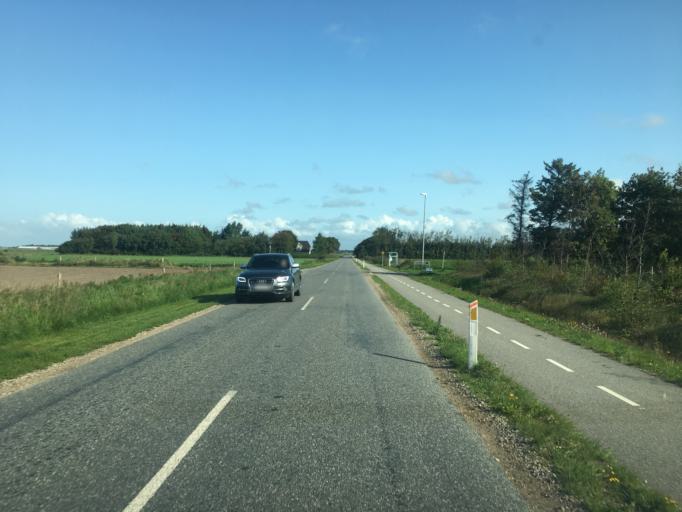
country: DK
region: South Denmark
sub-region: Tonder Kommune
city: Sherrebek
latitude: 55.1311
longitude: 8.7612
